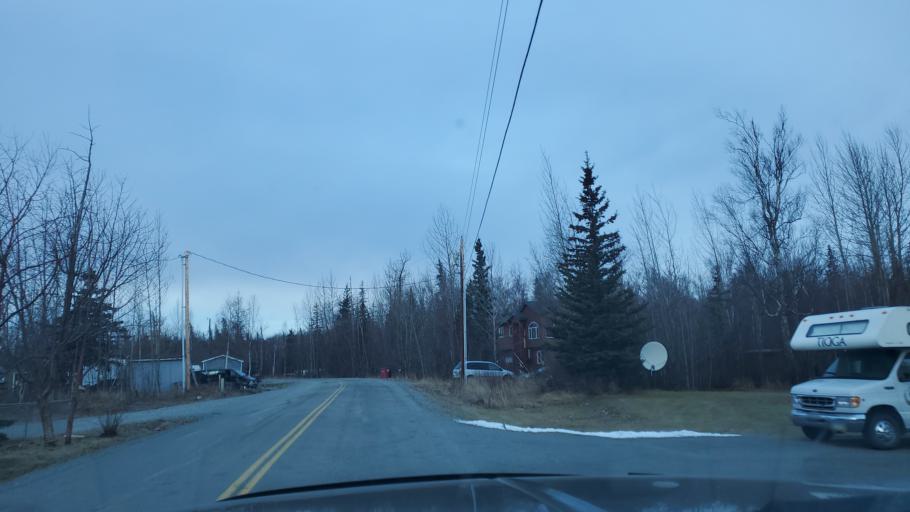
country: US
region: Alaska
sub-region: Matanuska-Susitna Borough
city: Lakes
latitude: 61.5728
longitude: -149.3367
